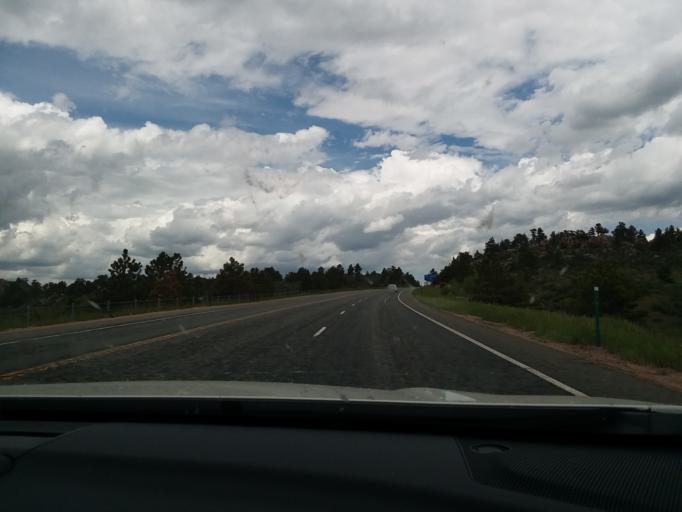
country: US
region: Wyoming
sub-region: Albany County
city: Laramie
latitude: 40.9689
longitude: -105.3802
